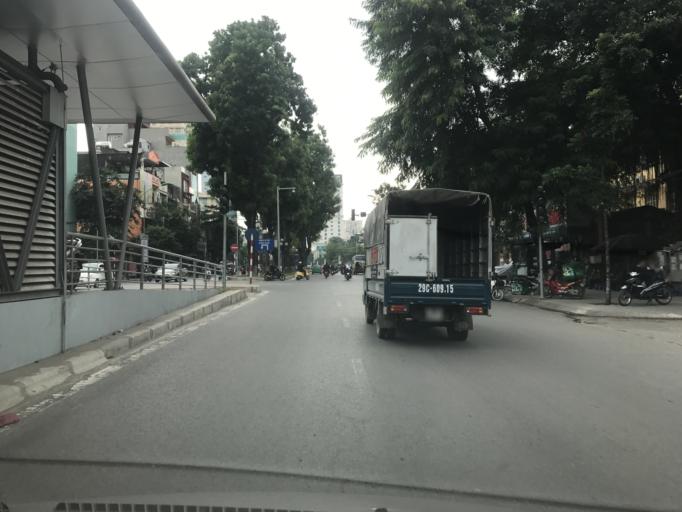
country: VN
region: Ha Noi
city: Dong Da
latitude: 21.0289
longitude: 105.8263
